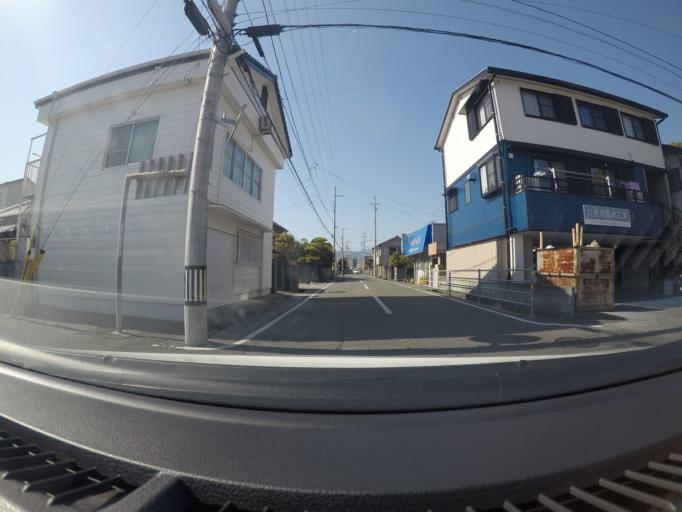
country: JP
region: Kochi
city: Kochi-shi
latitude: 33.5468
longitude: 133.5697
